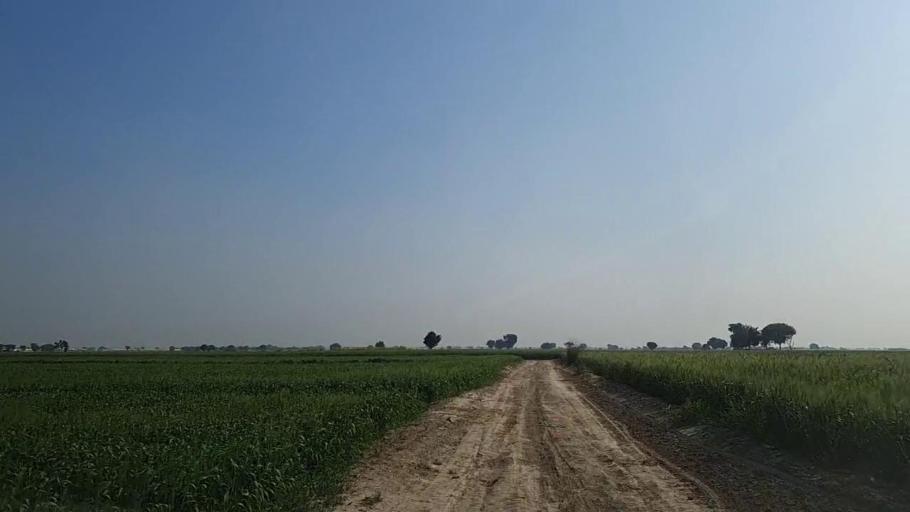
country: PK
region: Sindh
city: Moro
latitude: 26.6796
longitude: 67.9374
